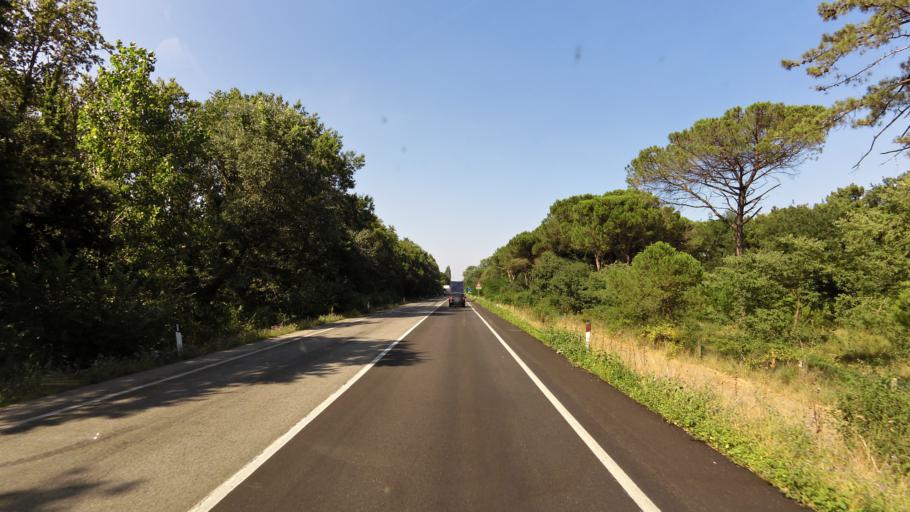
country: IT
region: Emilia-Romagna
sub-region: Provincia di Ravenna
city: Marina Romea
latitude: 44.5029
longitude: 12.2201
